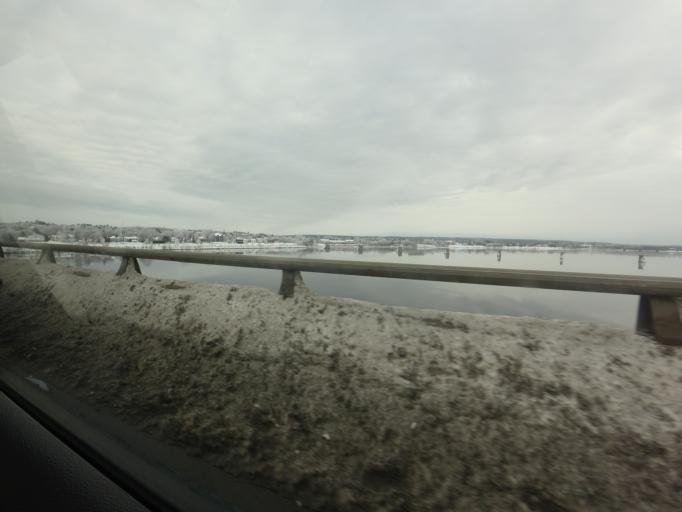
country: CA
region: New Brunswick
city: Fredericton
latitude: 45.9678
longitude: -66.6429
